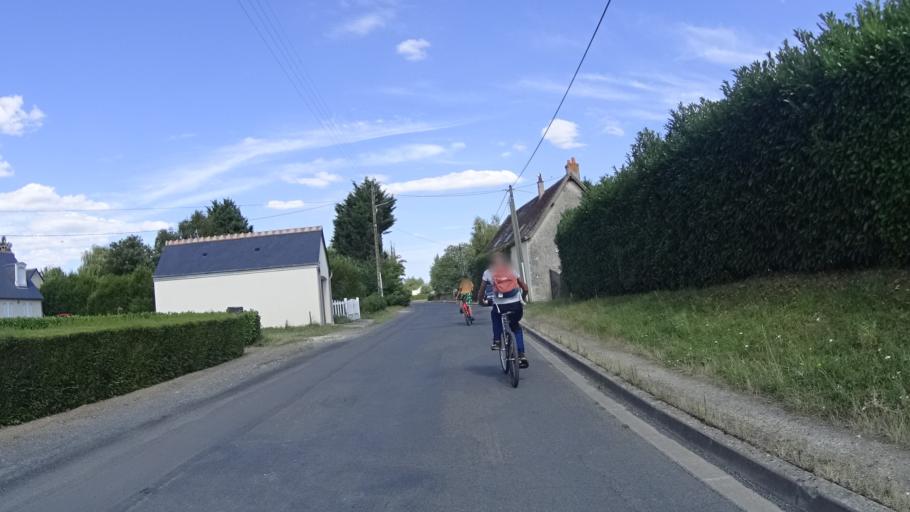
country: FR
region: Centre
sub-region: Departement d'Indre-et-Loire
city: Nazelles-Negron
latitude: 47.4132
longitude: 0.9518
